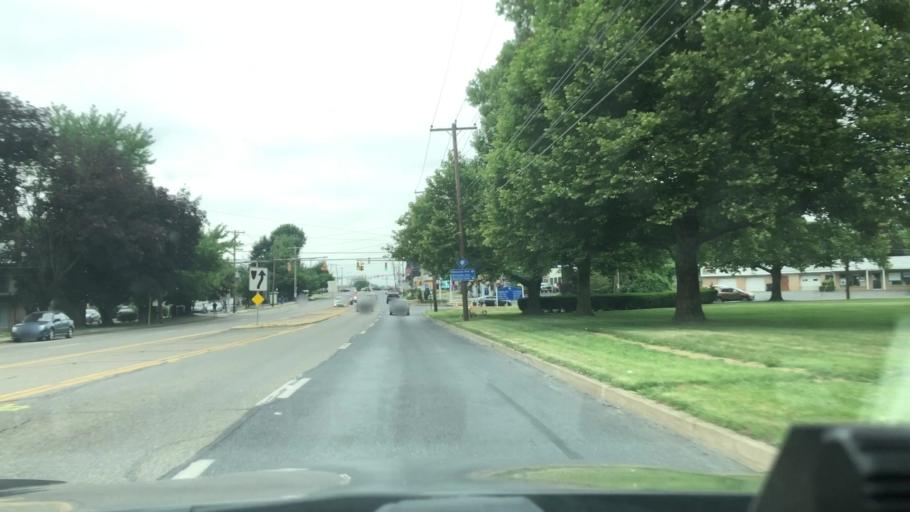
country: US
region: Pennsylvania
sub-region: Northampton County
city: Bethlehem
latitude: 40.6378
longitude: -75.3968
